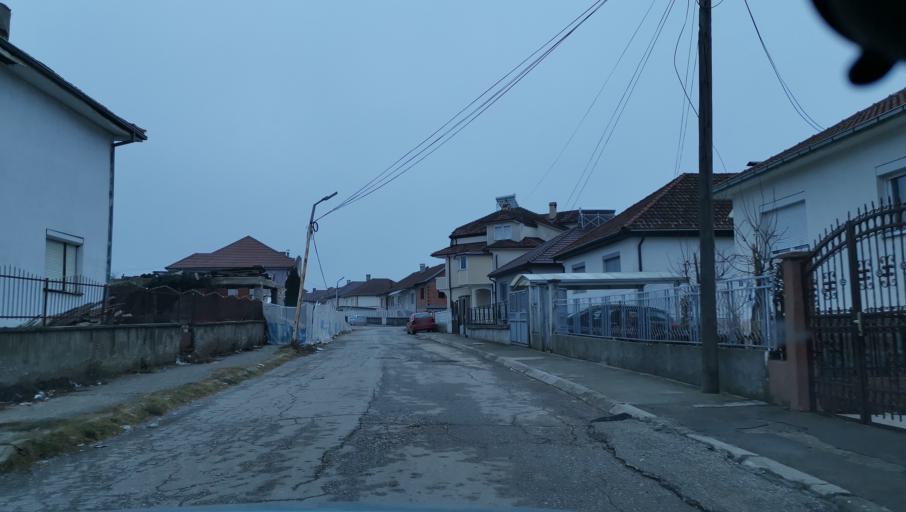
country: MK
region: Debar
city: Debar
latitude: 41.5171
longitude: 20.5303
